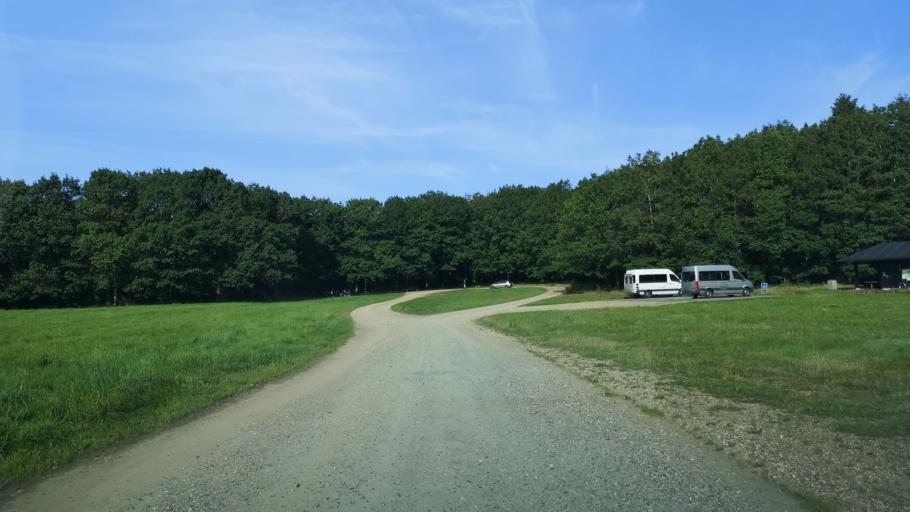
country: DK
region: Central Jutland
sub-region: Herning Kommune
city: Herning
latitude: 56.1781
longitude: 8.9499
